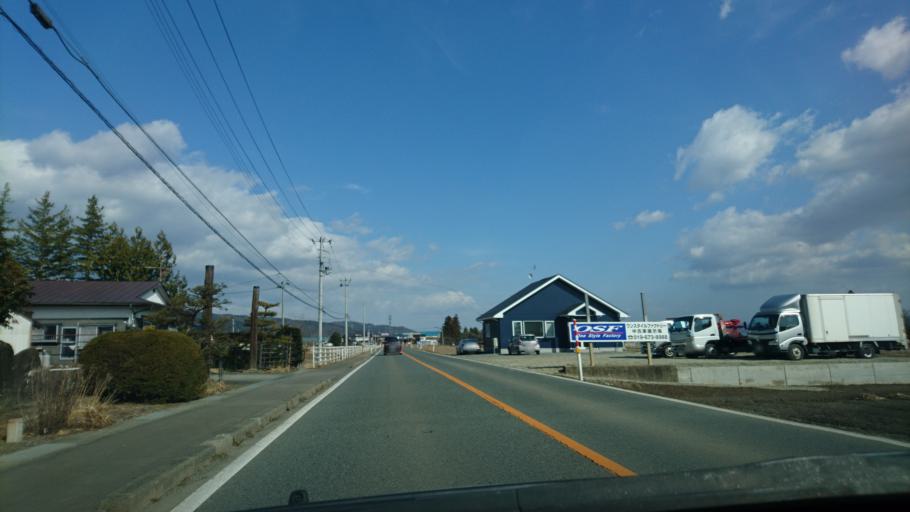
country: JP
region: Iwate
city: Morioka-shi
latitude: 39.5642
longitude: 141.1084
